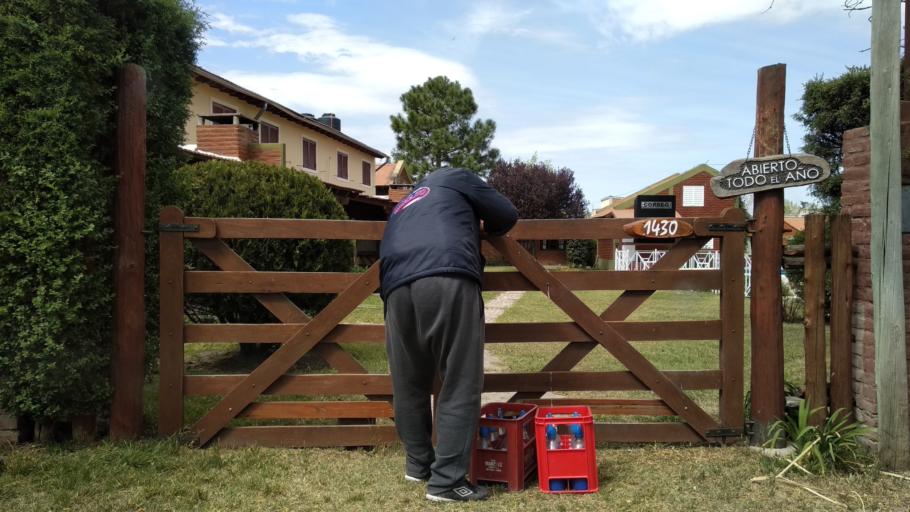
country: AR
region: Cordoba
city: Mina Clavero
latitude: -31.7303
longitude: -65.0153
